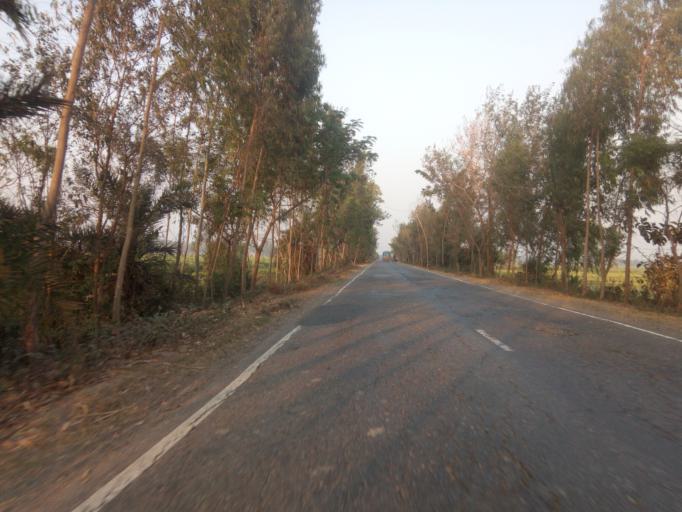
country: BD
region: Rajshahi
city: Bogra
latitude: 24.5786
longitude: 89.2226
